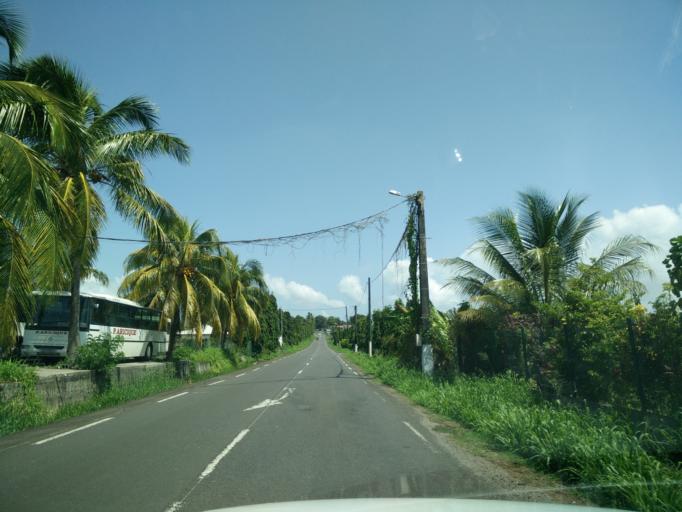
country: GP
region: Guadeloupe
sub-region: Guadeloupe
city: Petit-Bourg
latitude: 16.1787
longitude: -61.5872
